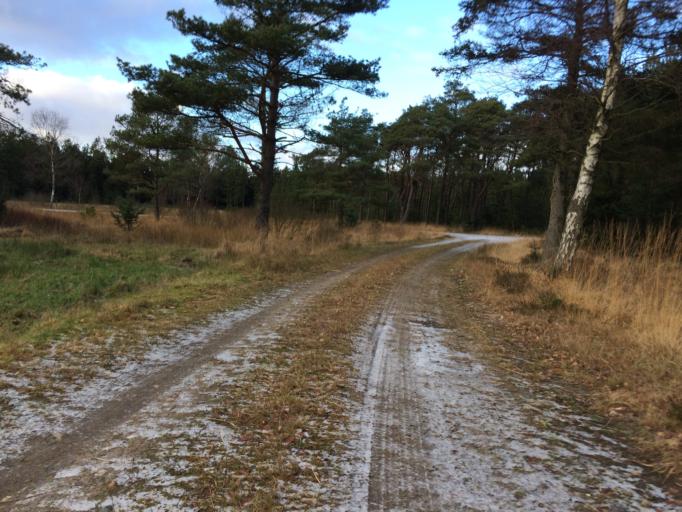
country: DK
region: Central Jutland
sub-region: Holstebro Kommune
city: Ulfborg
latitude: 56.2661
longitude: 8.3918
